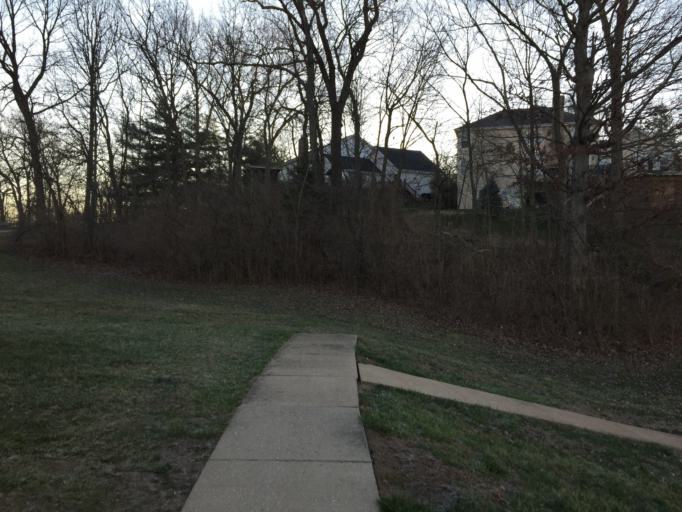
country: US
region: Missouri
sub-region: Saint Louis County
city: Ellisville
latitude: 38.5822
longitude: -90.6089
